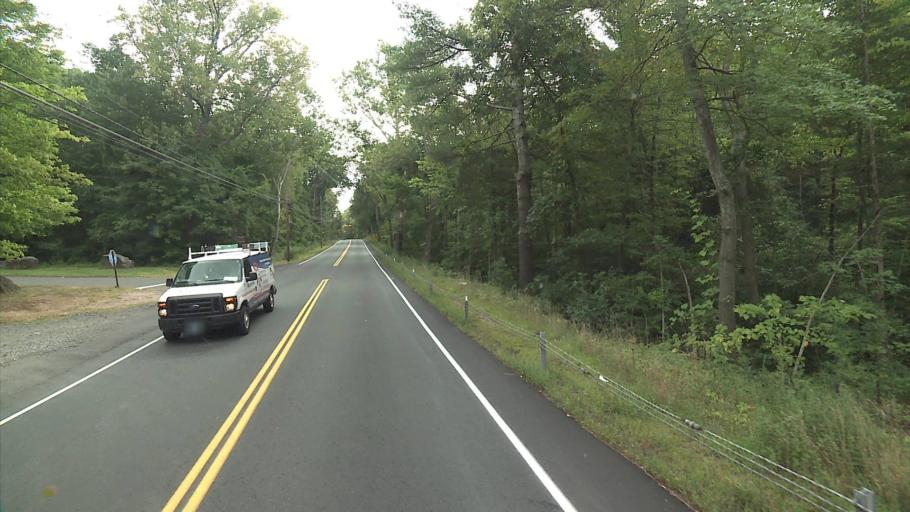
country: US
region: Connecticut
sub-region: Hartford County
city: Weatogue
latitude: 41.8384
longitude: -72.7867
